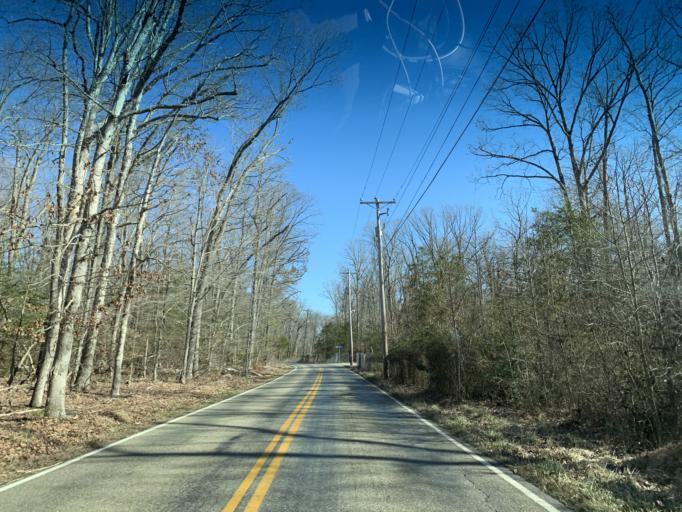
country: US
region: Maryland
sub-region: Cecil County
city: Charlestown
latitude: 39.4951
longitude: -75.8861
